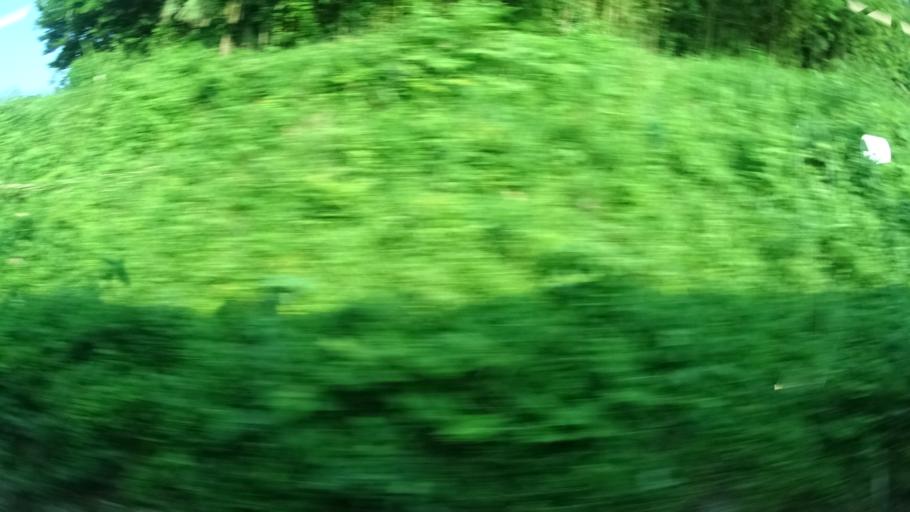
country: JP
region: Ibaraki
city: Takahagi
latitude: 36.6791
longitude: 140.6918
